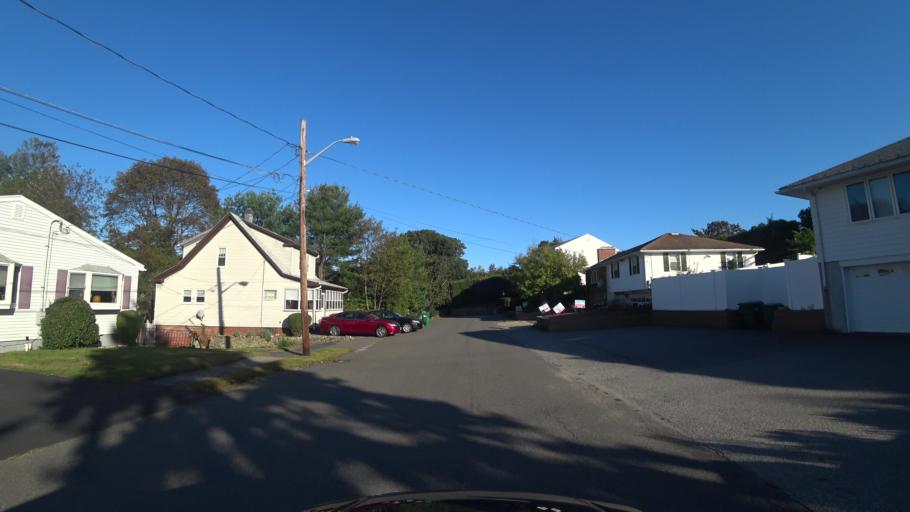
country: US
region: Massachusetts
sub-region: Middlesex County
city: Medford
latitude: 42.4371
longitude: -71.0889
